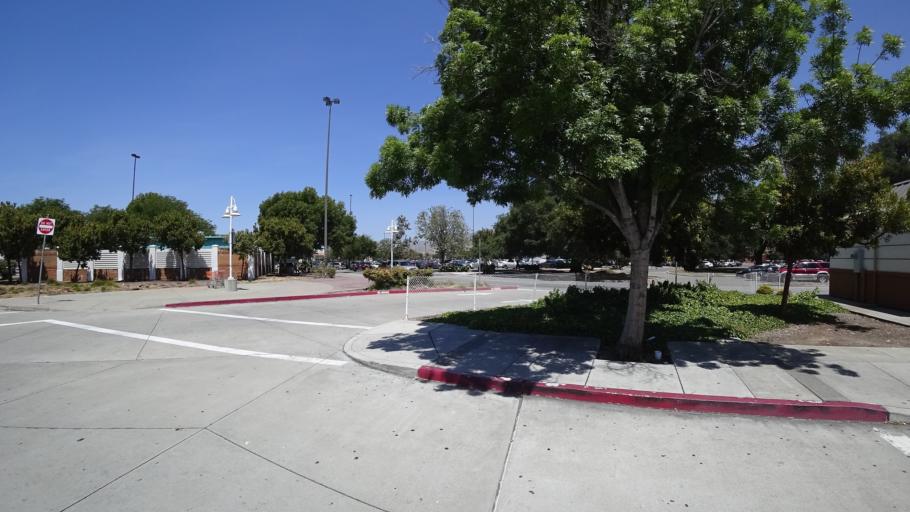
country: US
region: California
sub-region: Santa Clara County
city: Milpitas
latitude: 37.4140
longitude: -121.9003
